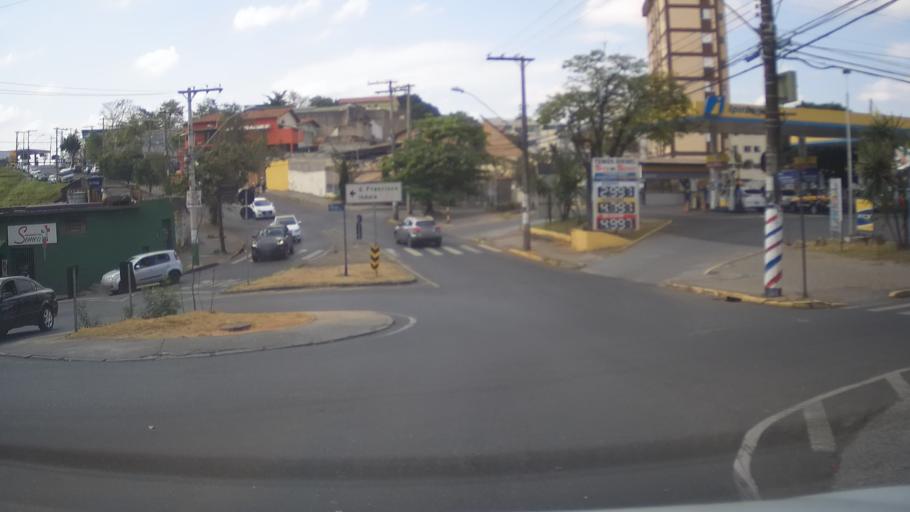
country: BR
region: Minas Gerais
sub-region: Belo Horizonte
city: Belo Horizonte
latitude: -19.8702
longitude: -43.9494
